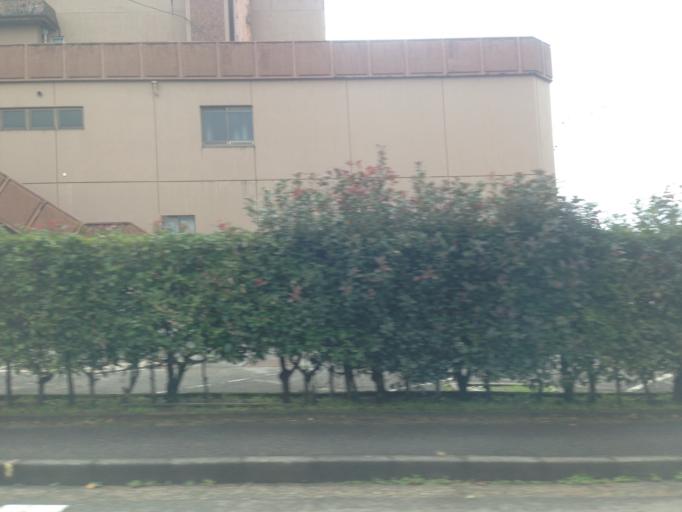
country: JP
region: Ishikawa
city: Komatsu
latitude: 36.2875
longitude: 136.3547
